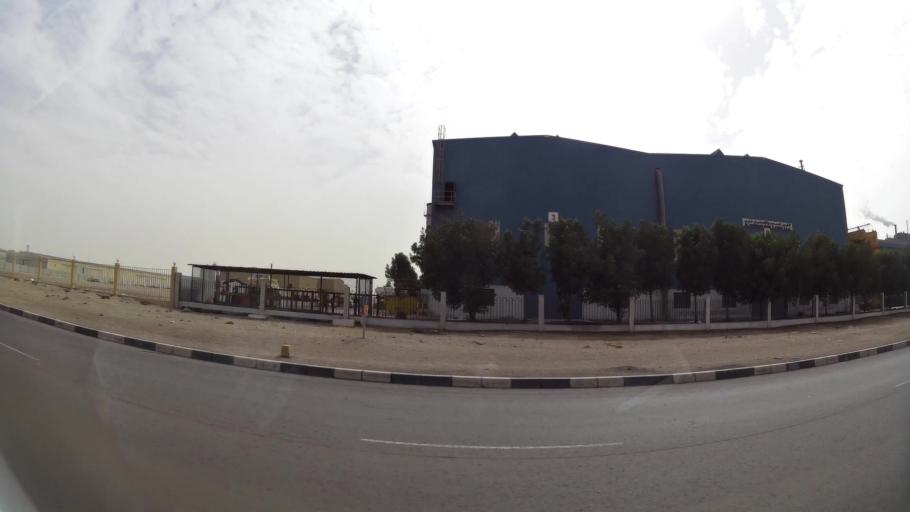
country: AE
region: Abu Dhabi
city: Abu Dhabi
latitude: 24.3225
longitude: 54.4819
